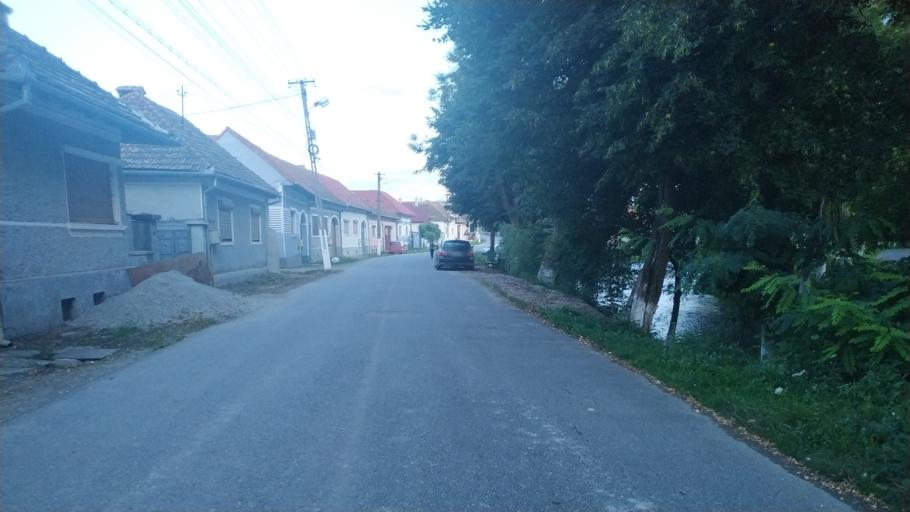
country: RO
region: Brasov
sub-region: Comuna Beclean
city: Beclean
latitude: 45.8304
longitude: 24.9244
